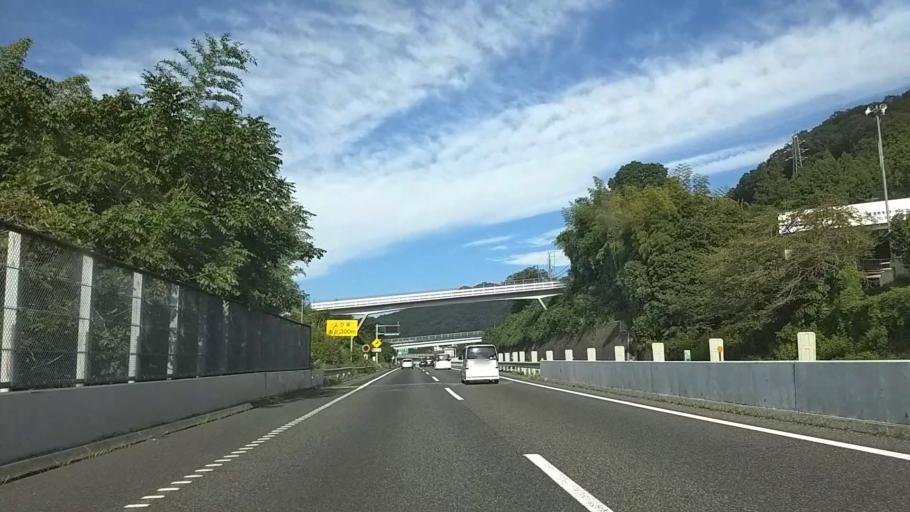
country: JP
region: Yamanashi
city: Uenohara
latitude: 35.6211
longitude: 139.1785
